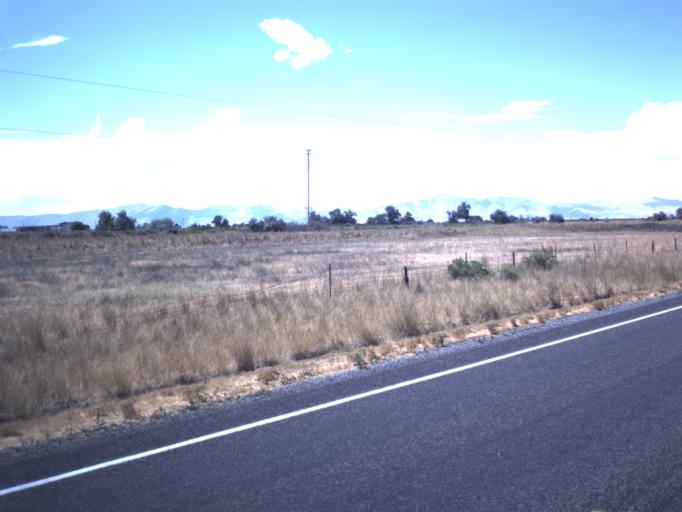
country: US
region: Utah
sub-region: Box Elder County
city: Honeyville
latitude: 41.5636
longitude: -112.1701
